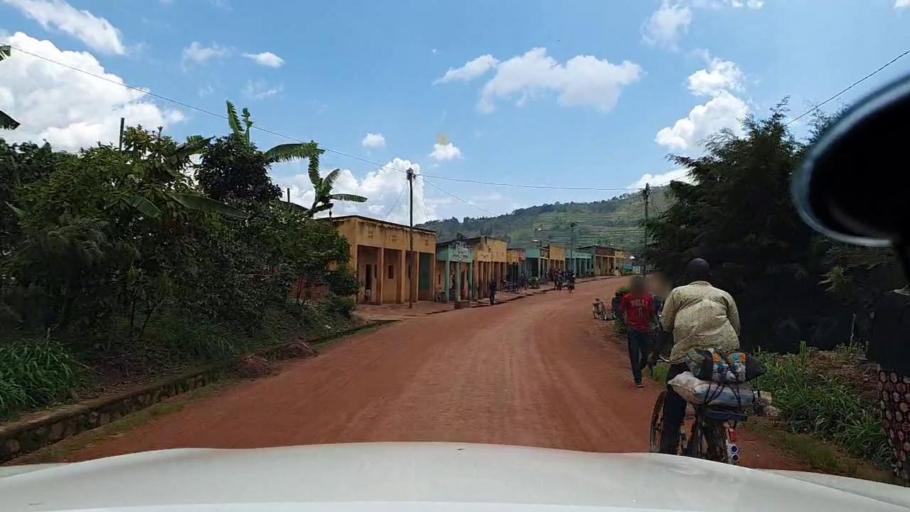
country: RW
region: Kigali
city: Kigali
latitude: -1.7721
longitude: 29.8425
